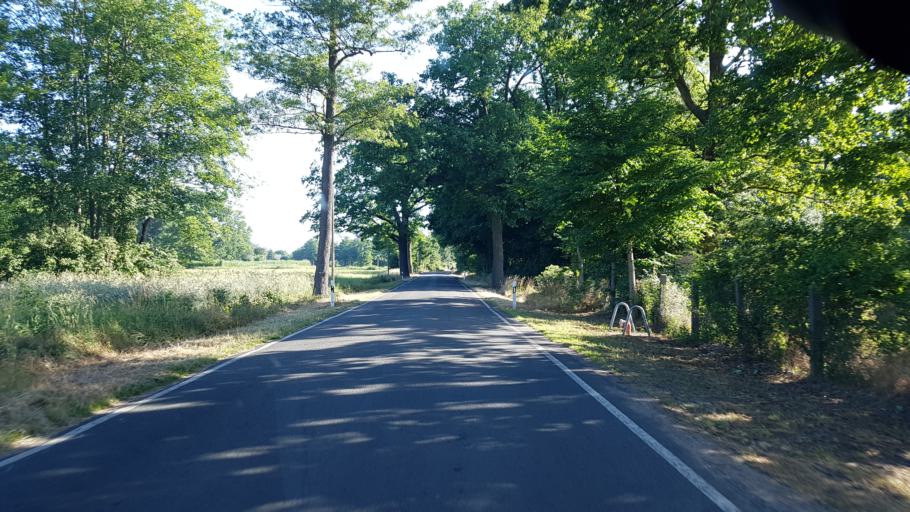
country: DE
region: Brandenburg
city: Kasel-Golzig
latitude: 51.9780
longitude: 13.6917
